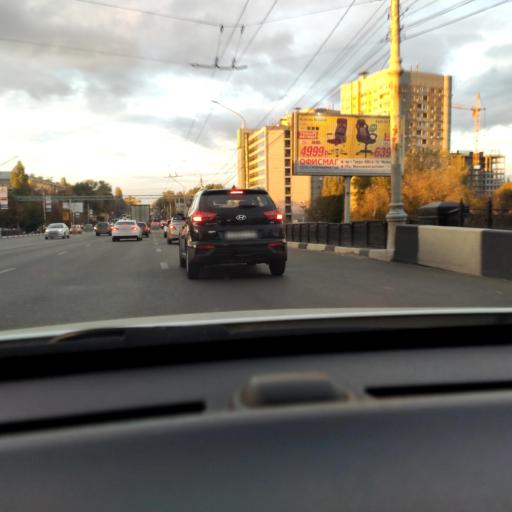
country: RU
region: Voronezj
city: Voronezh
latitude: 51.6771
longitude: 39.1837
